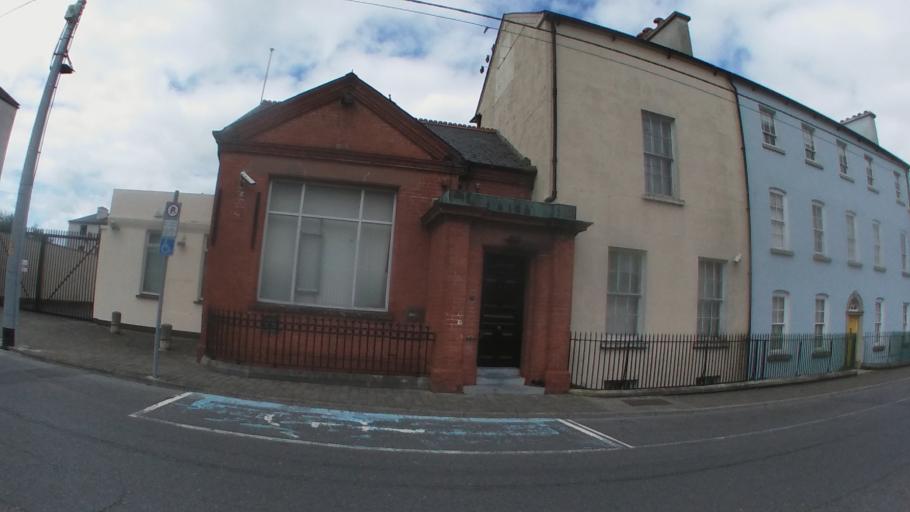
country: IE
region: Leinster
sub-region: County Carlow
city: Carlow
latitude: 52.8391
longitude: -6.9306
